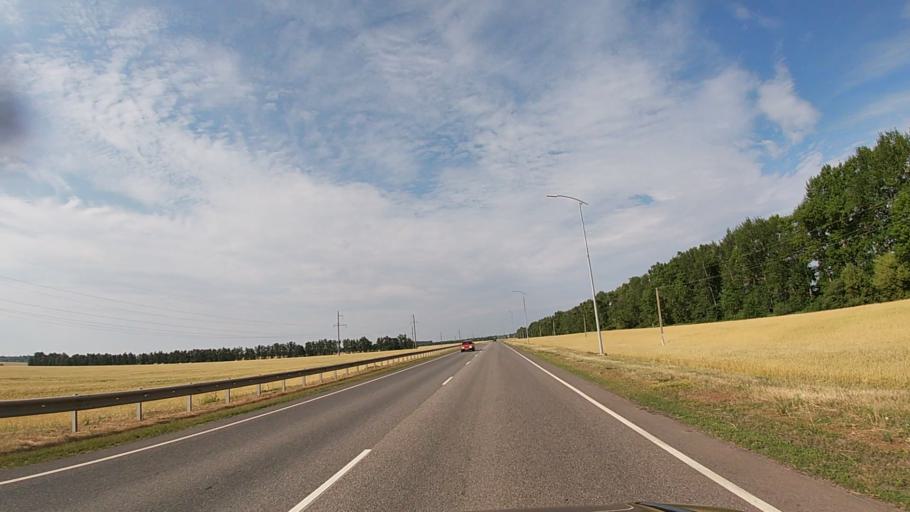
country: RU
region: Belgorod
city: Proletarskiy
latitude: 50.8167
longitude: 35.7529
